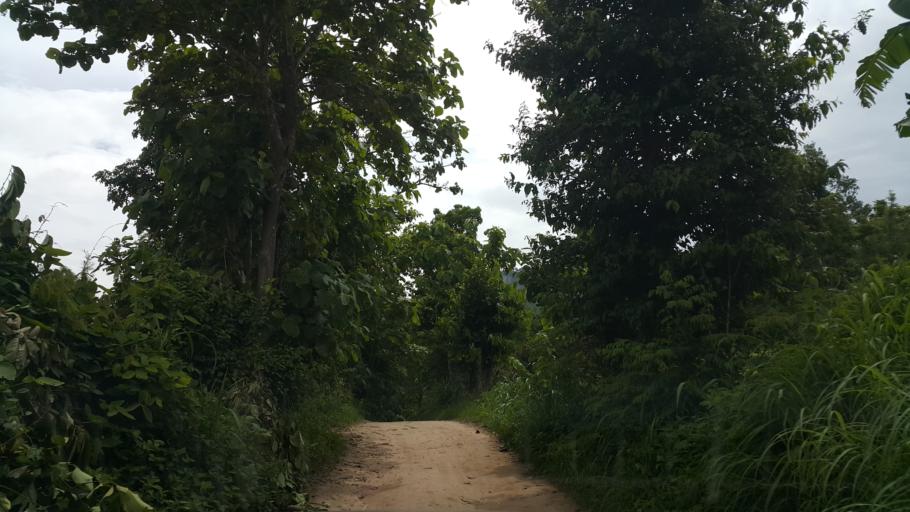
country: TH
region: Lampang
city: Chae Hom
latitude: 18.7462
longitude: 99.5583
